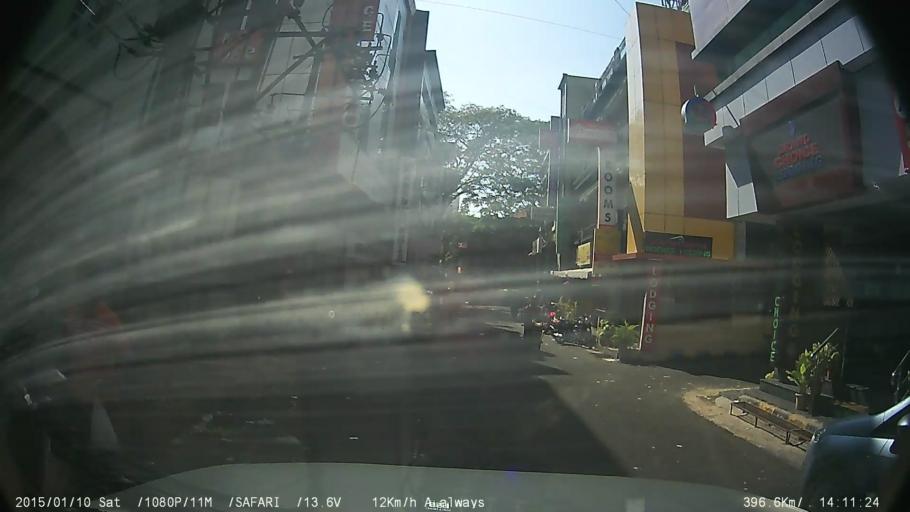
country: IN
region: Karnataka
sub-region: Bangalore Urban
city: Bangalore
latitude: 12.9267
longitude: 77.6163
